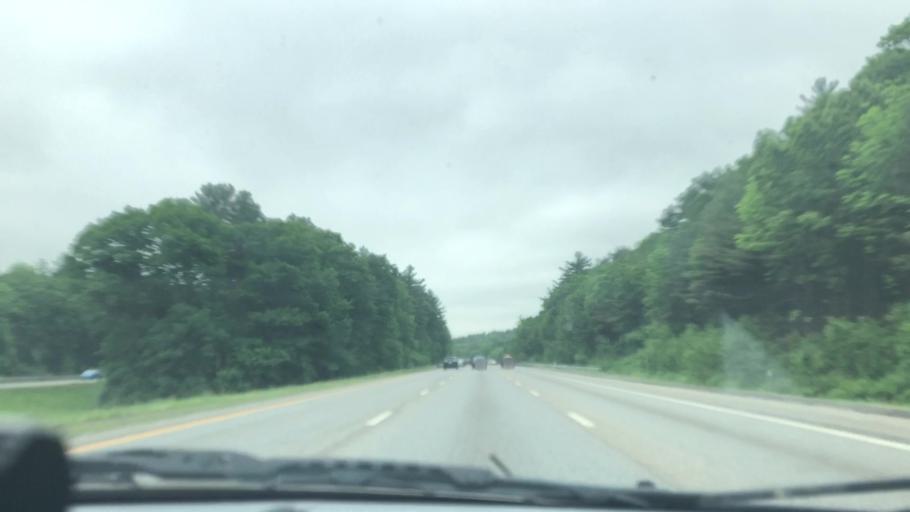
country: US
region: Massachusetts
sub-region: Worcester County
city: Harvard
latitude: 42.4683
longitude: -71.5605
